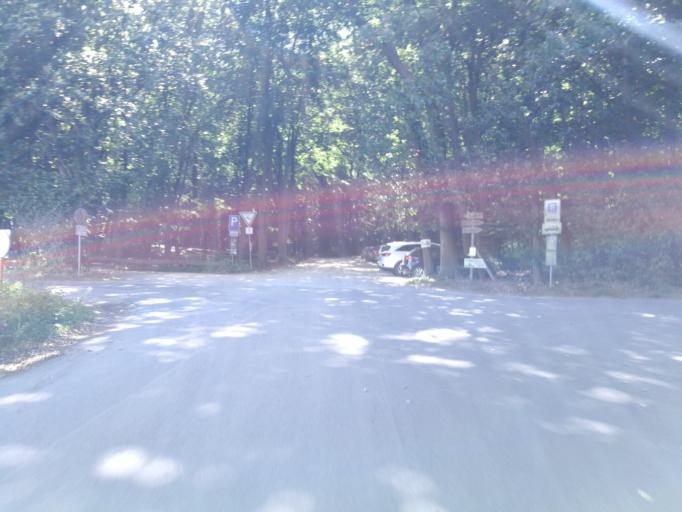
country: DE
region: North Rhine-Westphalia
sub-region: Regierungsbezirk Dusseldorf
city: Dormagen
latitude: 51.0833
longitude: 6.7892
